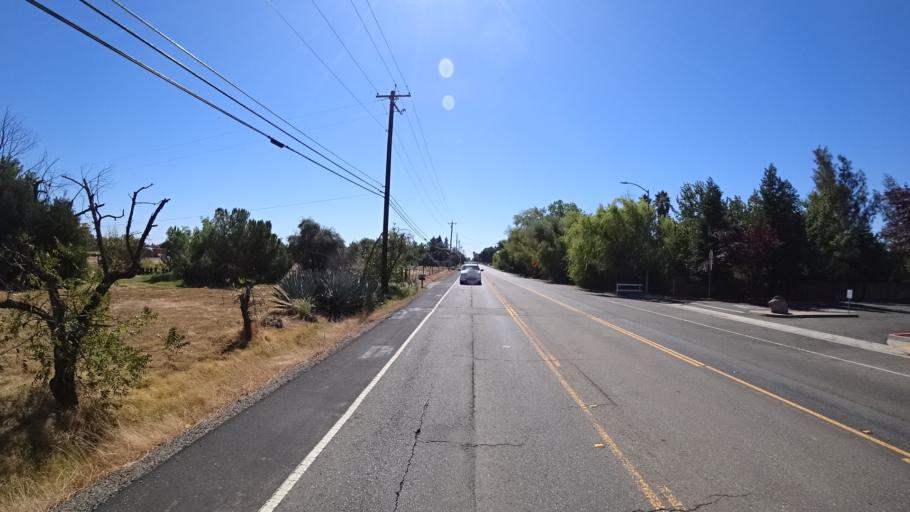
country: US
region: California
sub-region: Sacramento County
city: Vineyard
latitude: 38.4475
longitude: -121.3347
